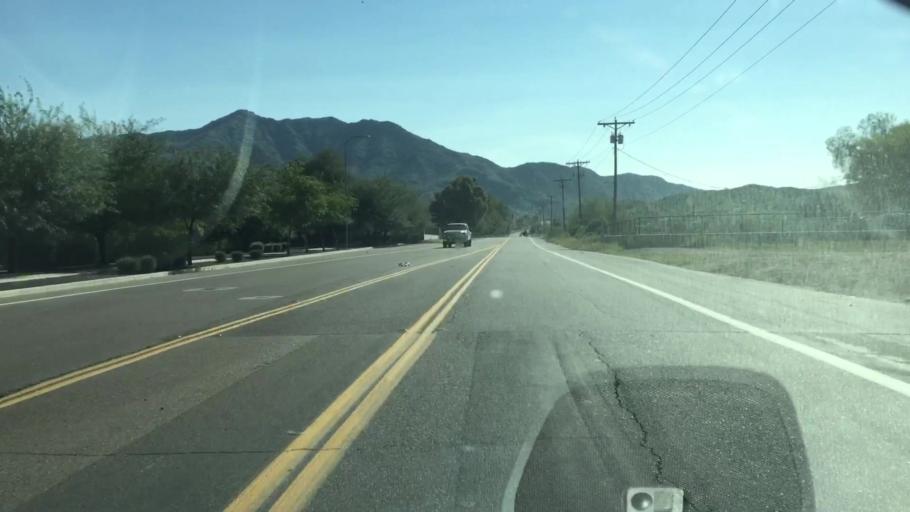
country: US
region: Arizona
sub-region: Maricopa County
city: Laveen
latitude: 33.3590
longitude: -112.1348
